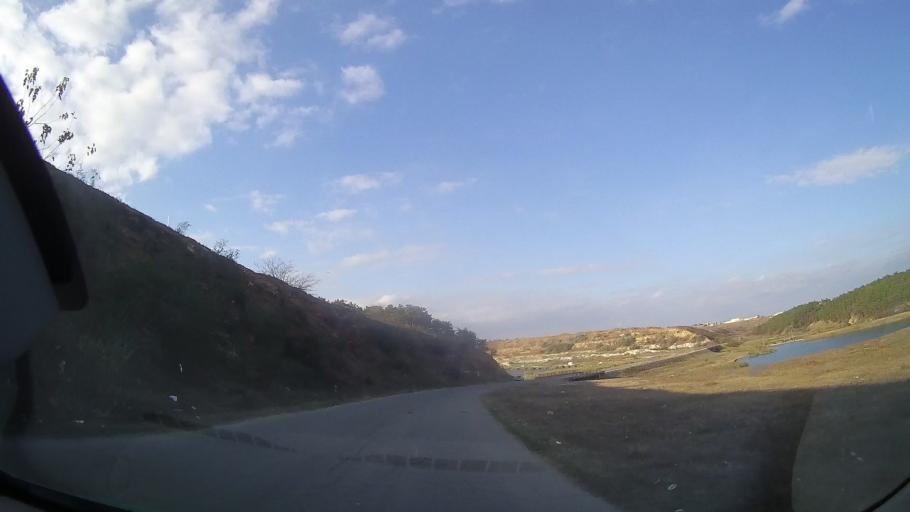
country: RO
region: Constanta
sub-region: Comuna Limanu
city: Limanu
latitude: 43.8110
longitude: 28.5175
